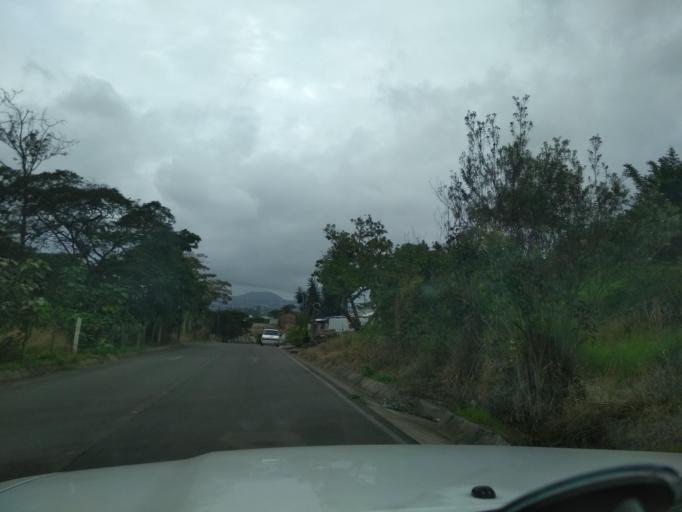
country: MX
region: Veracruz
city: El Castillo
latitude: 19.5477
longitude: -96.8444
